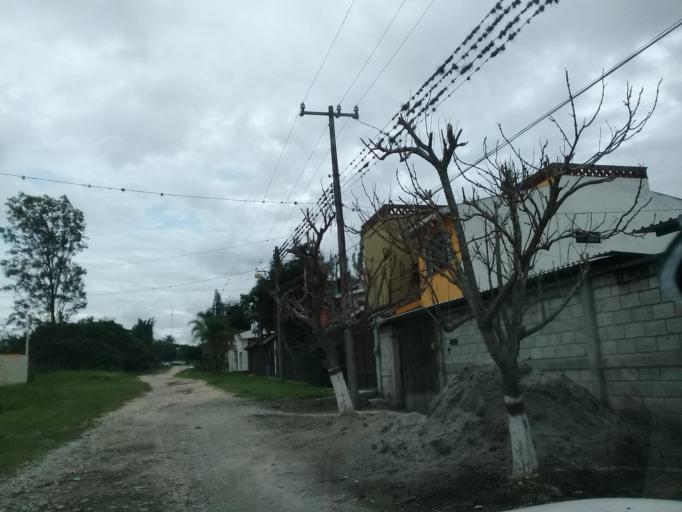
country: MX
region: Veracruz
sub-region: Emiliano Zapata
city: Dos Rios
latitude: 19.4840
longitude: -96.7929
